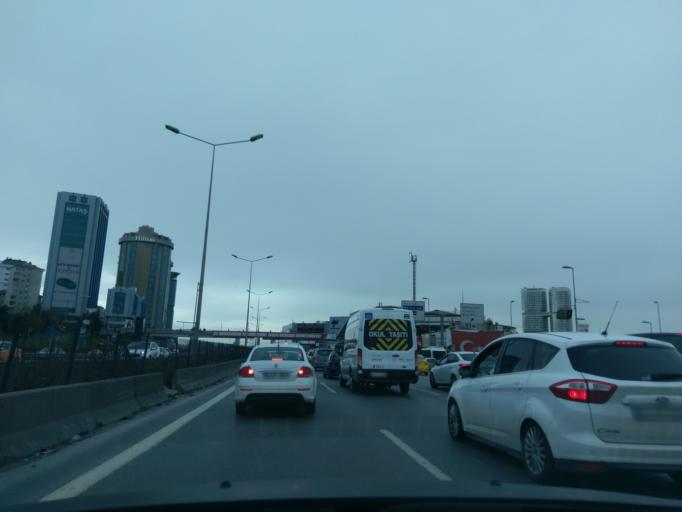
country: TR
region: Istanbul
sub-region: Atasehir
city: Atasehir
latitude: 40.9856
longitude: 29.0899
